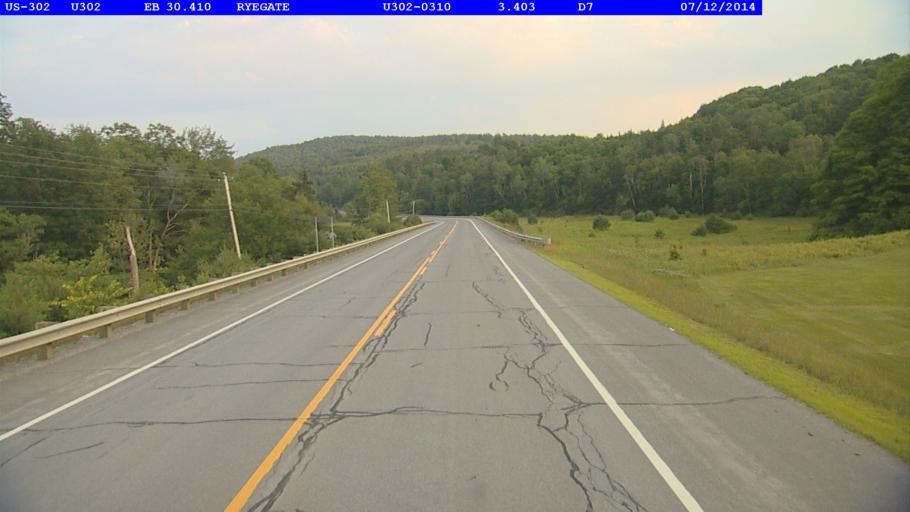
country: US
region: New Hampshire
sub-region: Grafton County
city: Woodsville
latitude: 44.1808
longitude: -72.1181
